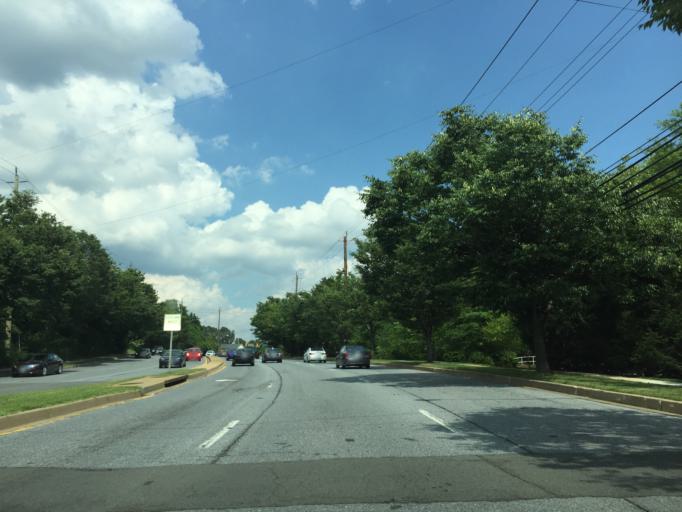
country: US
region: Maryland
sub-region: Montgomery County
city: Colesville
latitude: 39.0754
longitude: -76.9966
